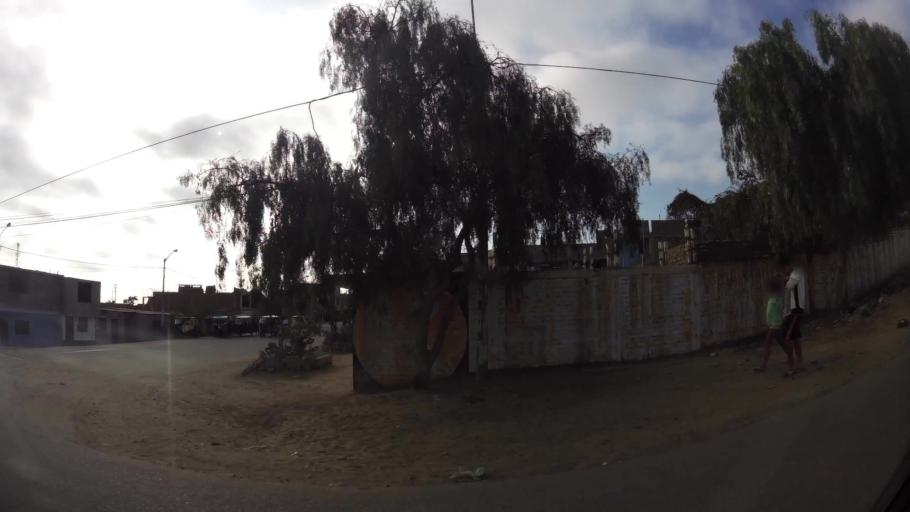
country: PE
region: La Libertad
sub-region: Provincia de Trujillo
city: La Esperanza
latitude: -8.0720
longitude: -79.0440
